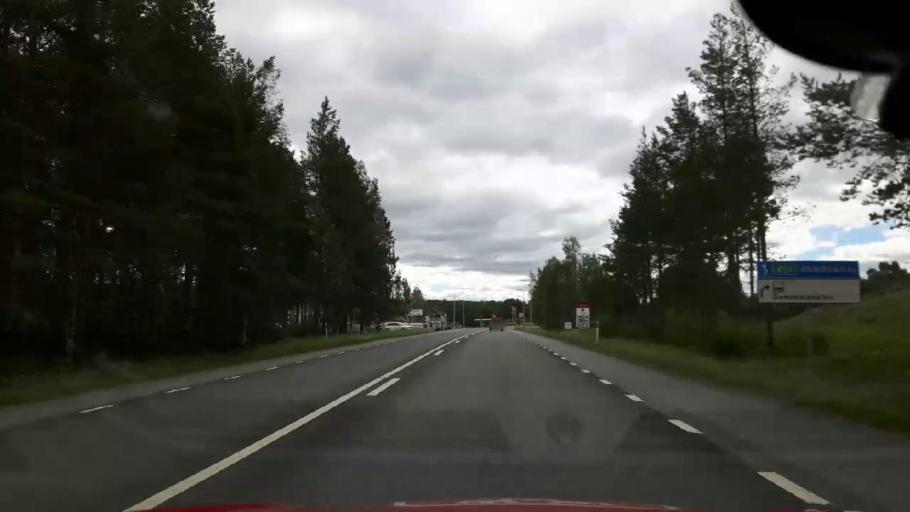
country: SE
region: Jaemtland
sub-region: Braecke Kommun
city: Braecke
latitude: 62.7585
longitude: 15.4115
